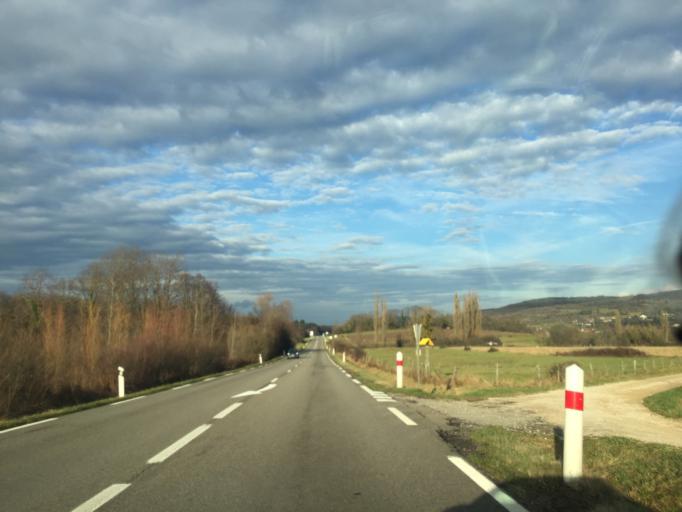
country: FR
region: Franche-Comte
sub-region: Departement du Jura
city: Arbois
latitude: 46.9362
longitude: 5.7772
